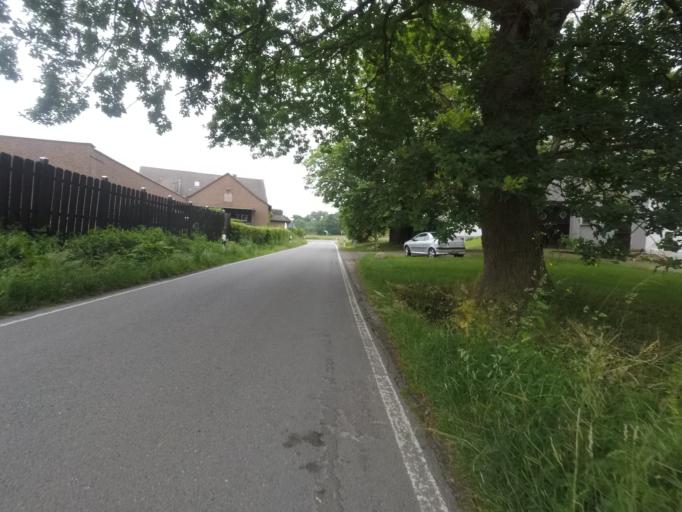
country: DE
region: North Rhine-Westphalia
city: Enger
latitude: 52.1618
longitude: 8.5647
